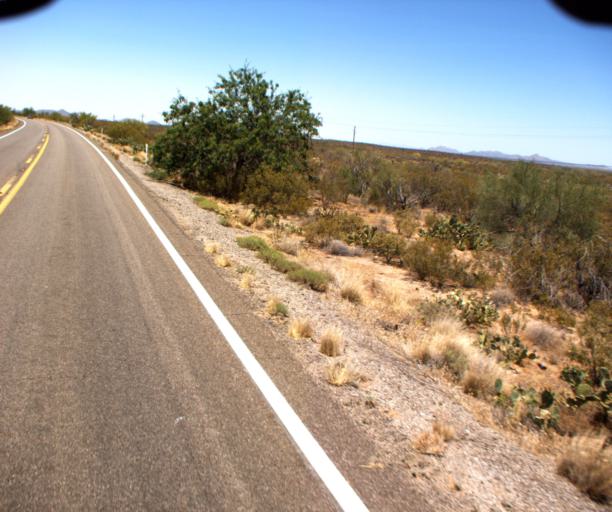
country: US
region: Arizona
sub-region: Pima County
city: Catalina
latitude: 32.6539
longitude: -111.0349
